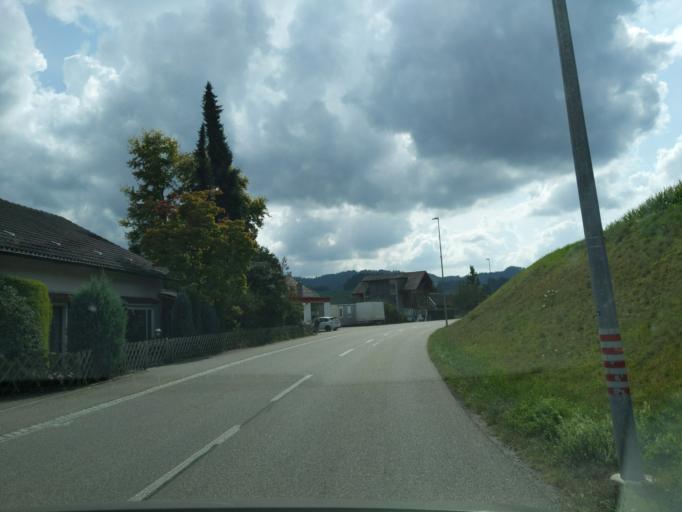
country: CH
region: Bern
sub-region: Oberaargau
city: Wyssachen
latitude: 47.0921
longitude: 7.8265
